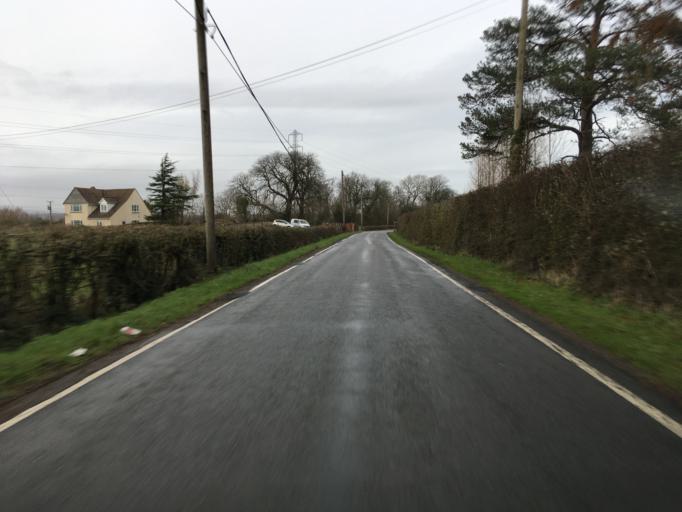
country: GB
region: Wales
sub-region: Newport
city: Goldcliff
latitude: 51.5585
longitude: -2.9100
